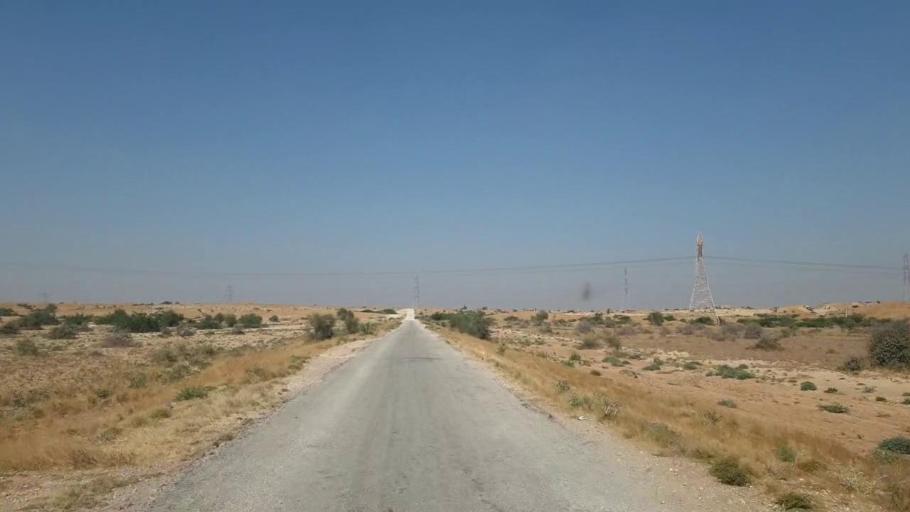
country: PK
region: Sindh
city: Thatta
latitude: 25.1949
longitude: 67.8006
